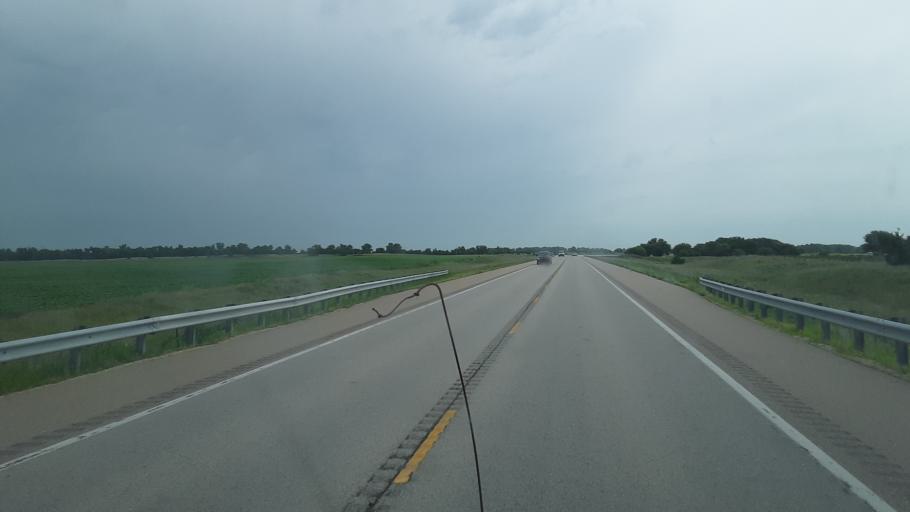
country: US
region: Kansas
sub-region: Stafford County
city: Stafford
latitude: 37.9784
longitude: -98.3944
